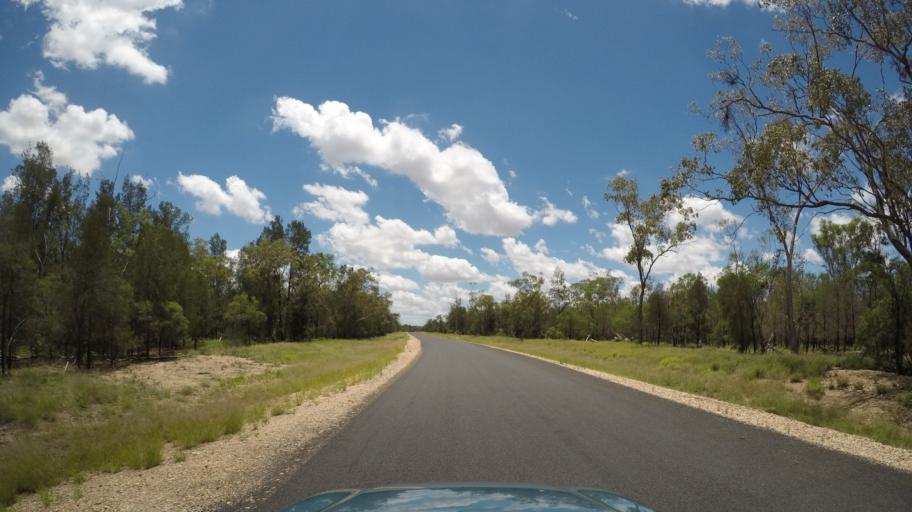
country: AU
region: Queensland
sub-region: Goondiwindi
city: Goondiwindi
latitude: -28.1548
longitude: 150.1227
